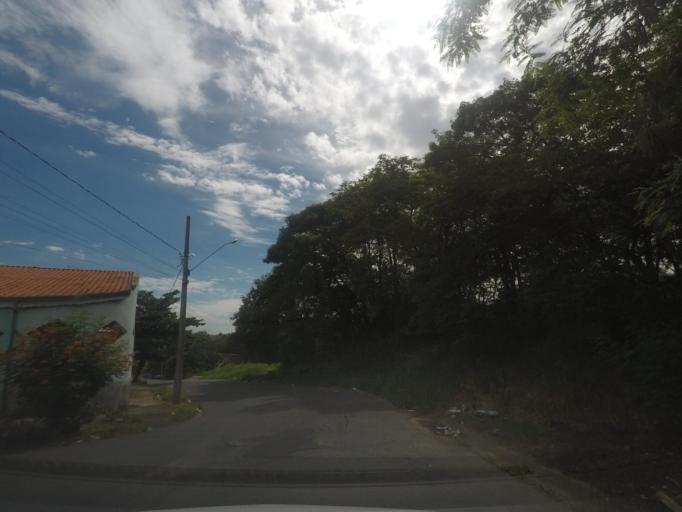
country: BR
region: Sao Paulo
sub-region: Sumare
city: Sumare
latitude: -22.8094
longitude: -47.2672
